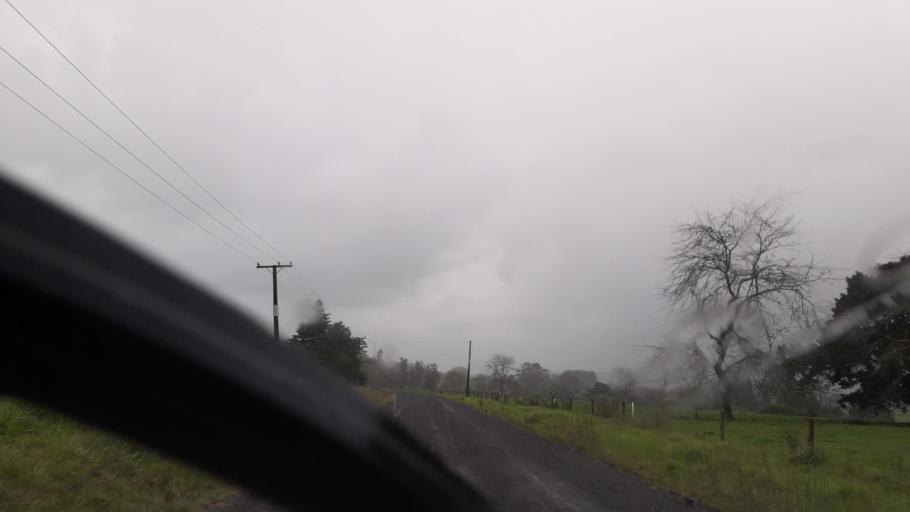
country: NZ
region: Northland
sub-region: Far North District
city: Waimate North
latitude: -35.4763
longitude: 173.6925
